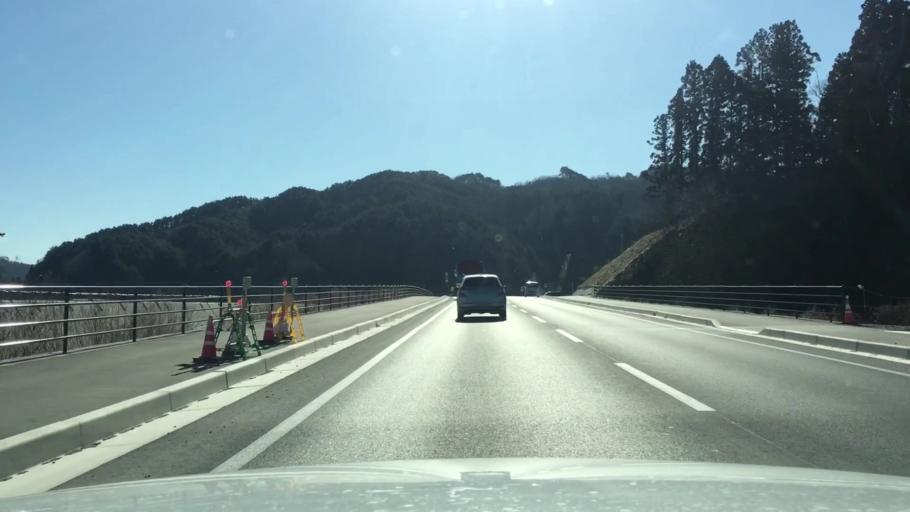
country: JP
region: Iwate
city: Yamada
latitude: 39.4524
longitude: 141.9613
